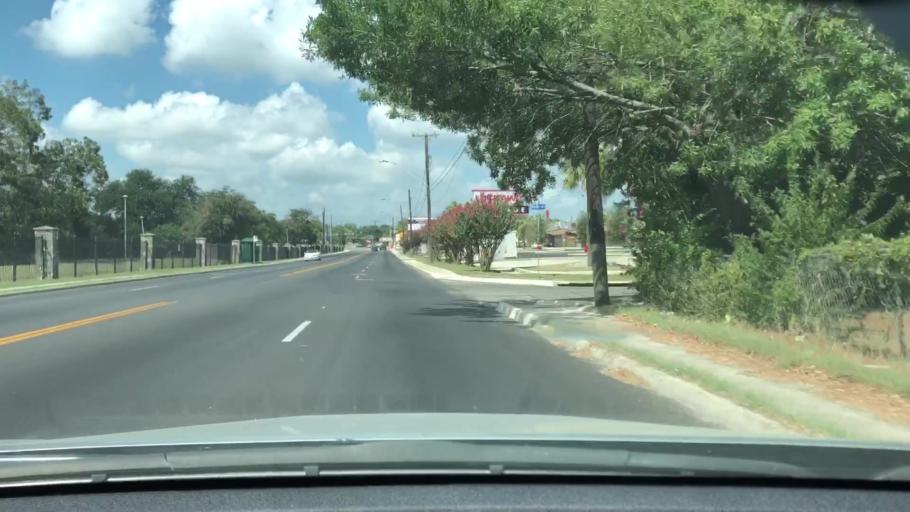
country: US
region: Texas
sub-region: Bexar County
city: Terrell Hills
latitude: 29.4849
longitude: -98.4263
